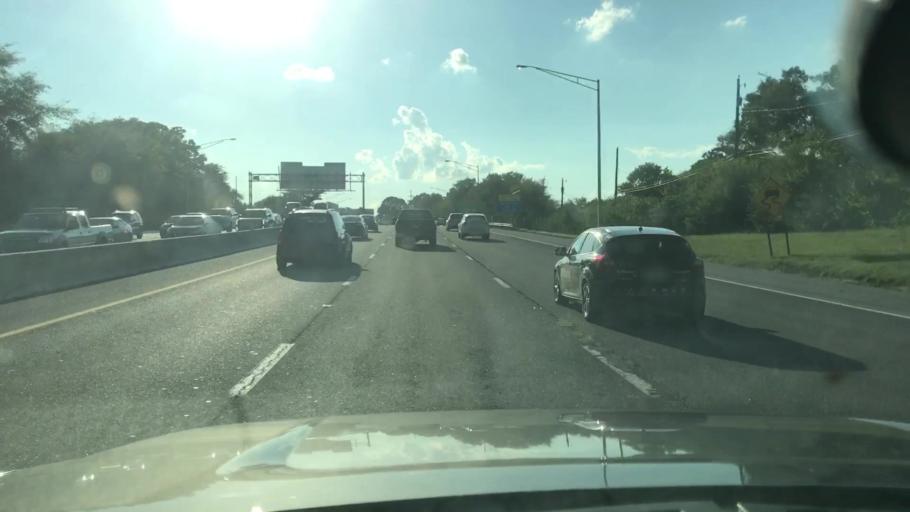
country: US
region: Tennessee
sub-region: Davidson County
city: Nashville
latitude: 36.1701
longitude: -86.8080
